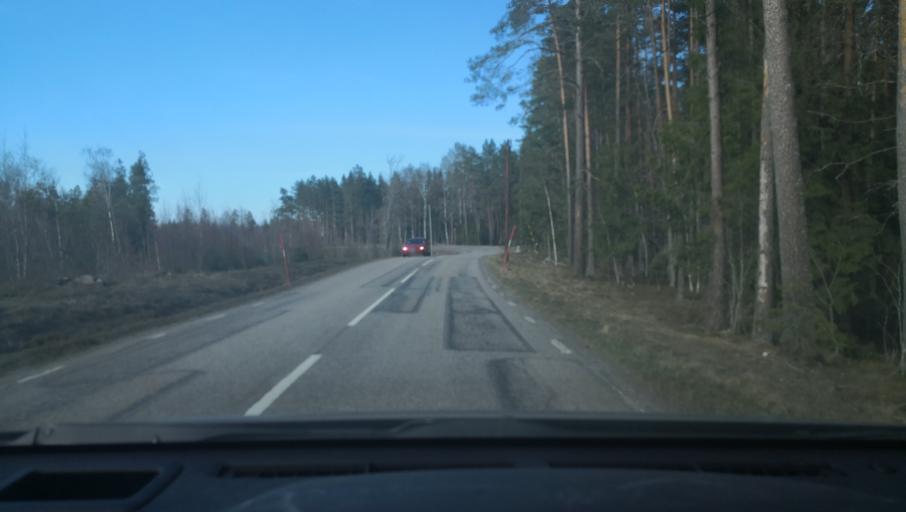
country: SE
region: Uppsala
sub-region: Heby Kommun
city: Morgongava
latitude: 59.9849
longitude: 16.9113
